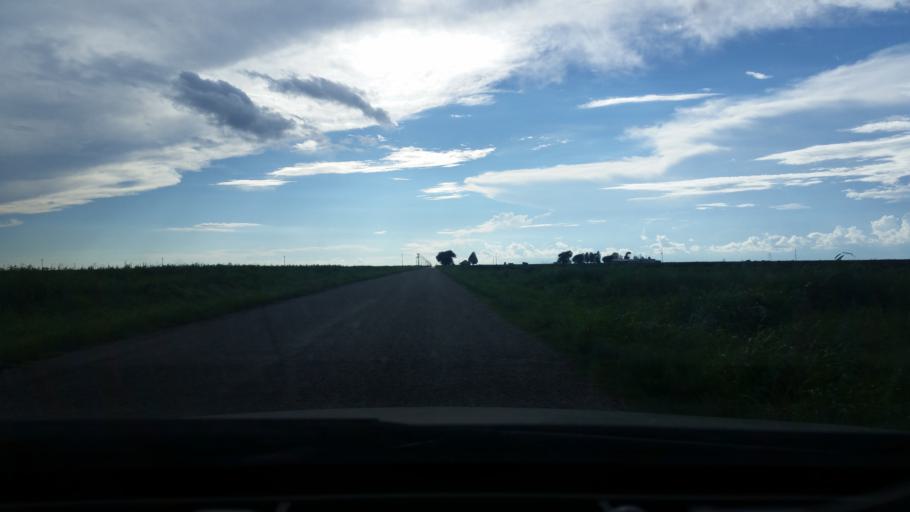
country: US
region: New Mexico
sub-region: Curry County
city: Clovis
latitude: 34.4630
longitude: -103.2255
